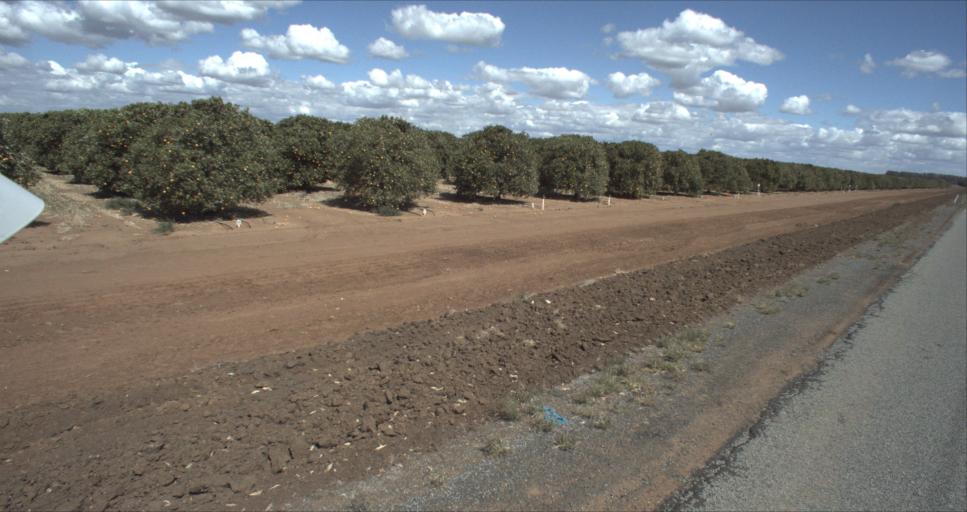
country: AU
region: New South Wales
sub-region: Leeton
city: Leeton
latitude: -34.5202
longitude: 146.2244
